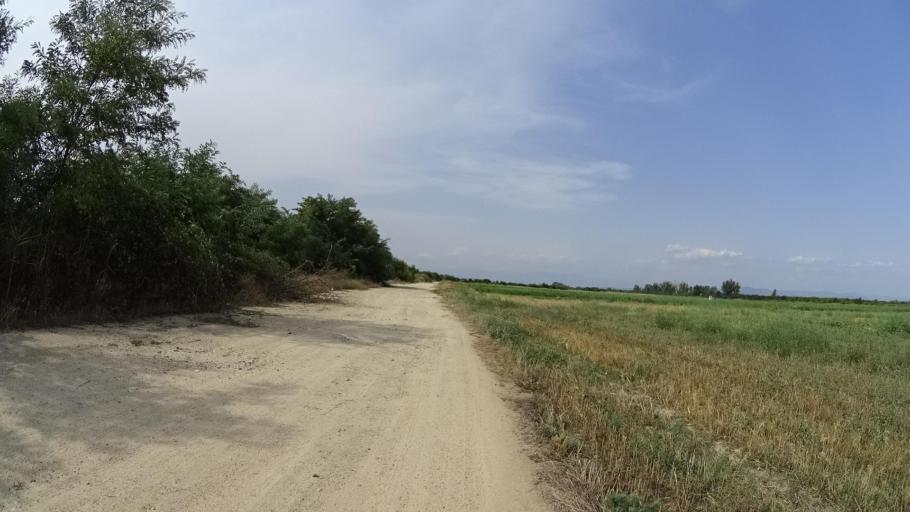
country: BG
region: Plovdiv
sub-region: Obshtina Kaloyanovo
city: Kaloyanovo
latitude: 42.2922
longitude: 24.7961
